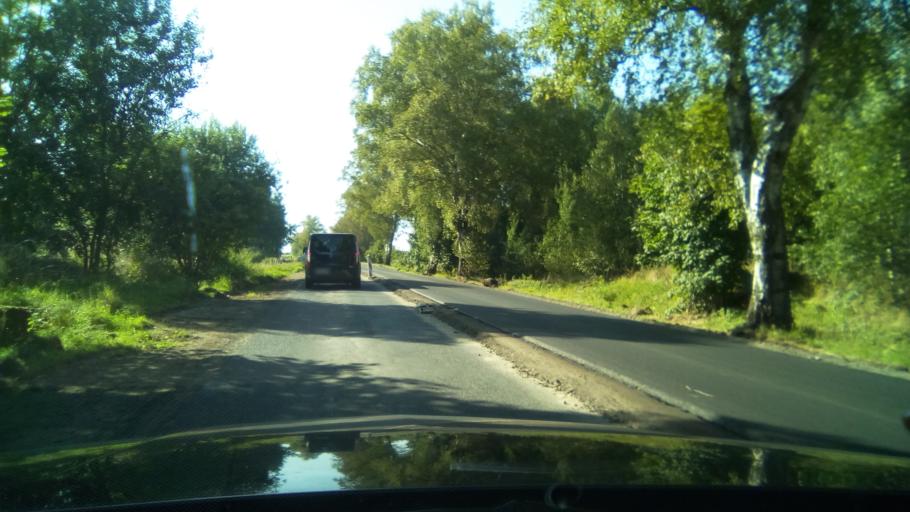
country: PL
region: West Pomeranian Voivodeship
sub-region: Powiat gryficki
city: Ploty
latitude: 53.8126
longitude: 15.1881
